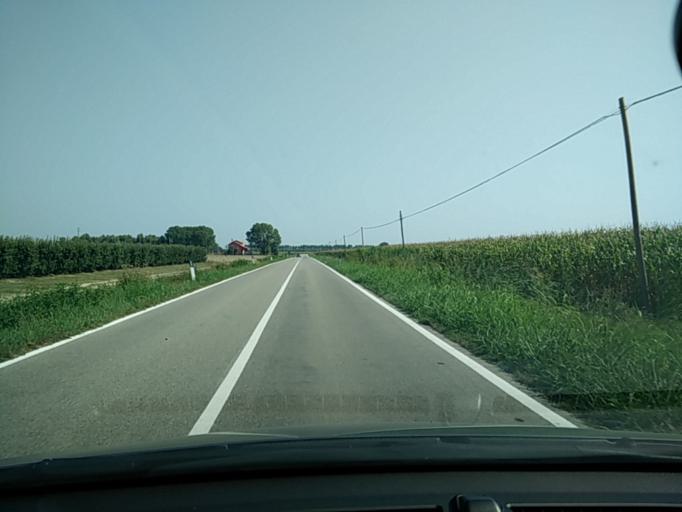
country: IT
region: Veneto
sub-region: Provincia di Venezia
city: La Salute di Livenza
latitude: 45.6304
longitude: 12.8357
